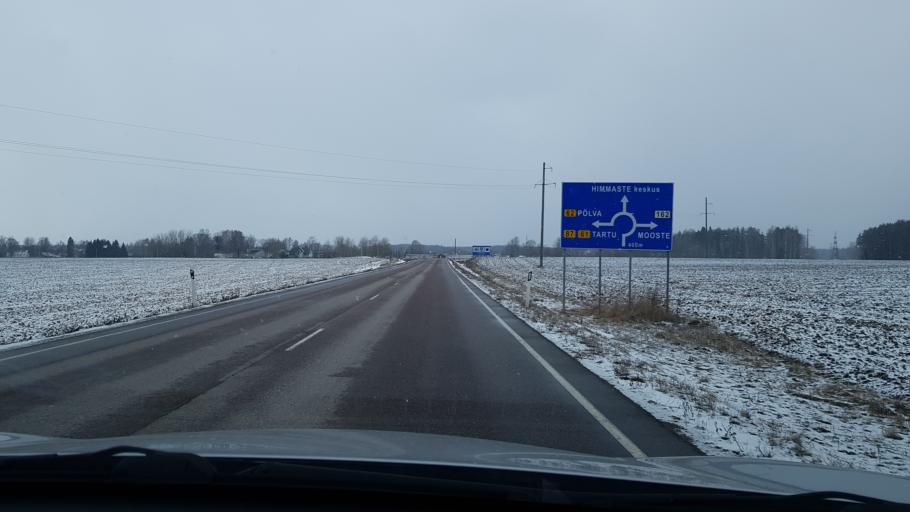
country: EE
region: Polvamaa
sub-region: Polva linn
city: Polva
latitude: 58.0896
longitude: 27.1003
